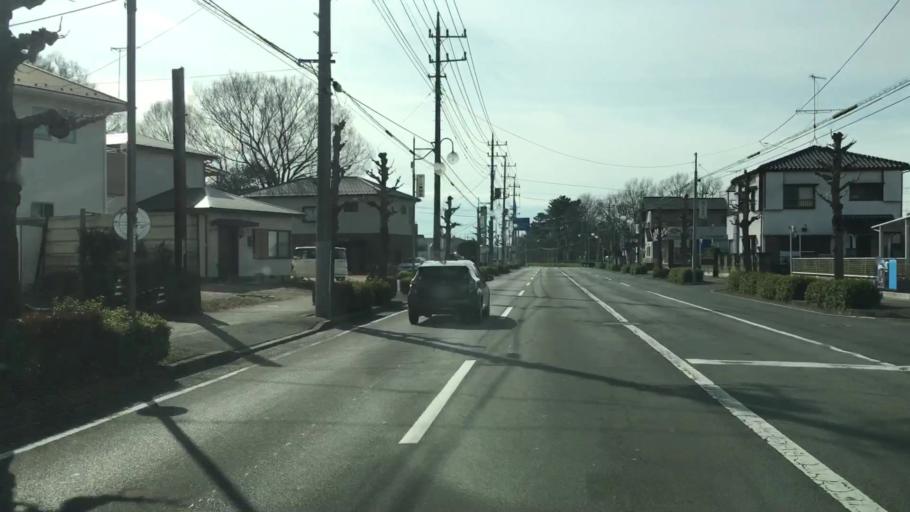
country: JP
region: Saitama
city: Menuma
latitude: 36.2472
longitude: 139.4100
